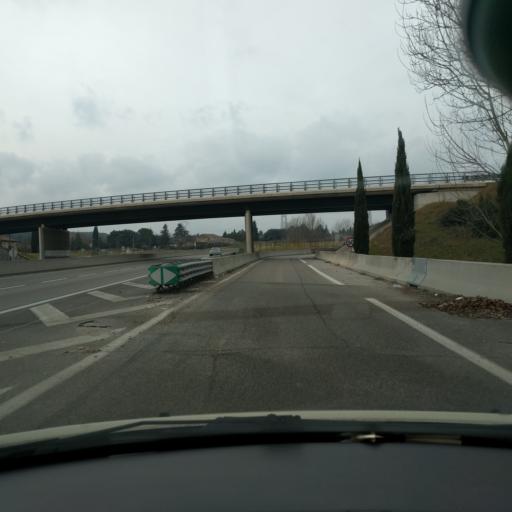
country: FR
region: Provence-Alpes-Cote d'Azur
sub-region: Departement des Bouches-du-Rhone
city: Meyreuil
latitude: 43.4747
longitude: 5.5178
